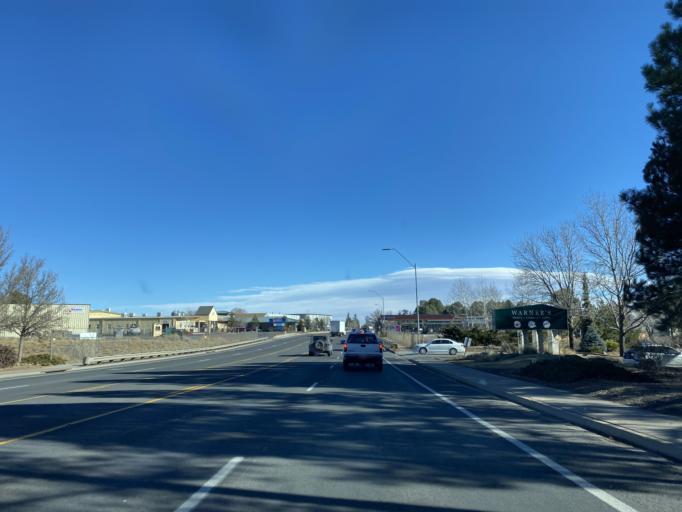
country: US
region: Arizona
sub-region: Coconino County
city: Flagstaff
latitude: 35.1917
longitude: -111.6372
